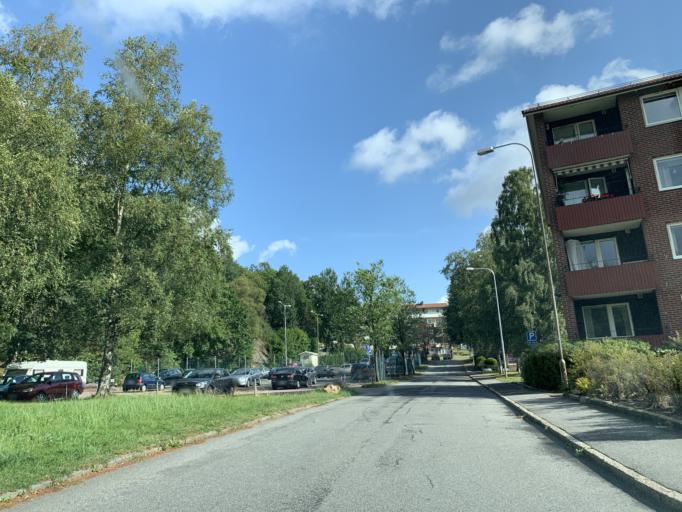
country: SE
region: Vaestra Goetaland
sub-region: Goteborg
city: Eriksbo
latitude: 57.7439
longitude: 12.0266
